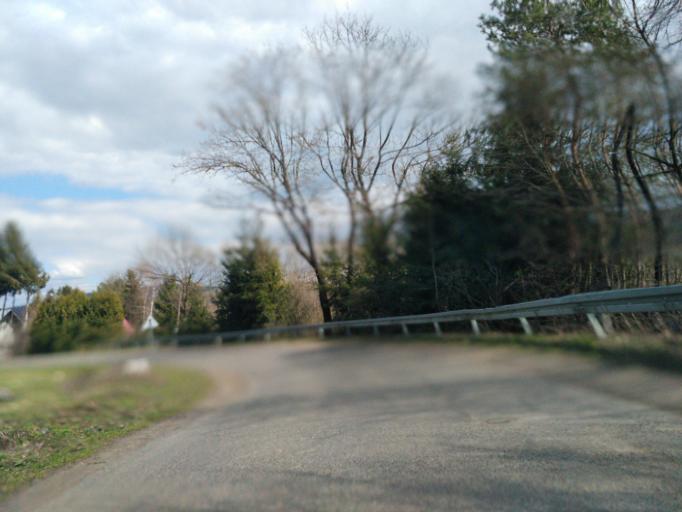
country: PL
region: Subcarpathian Voivodeship
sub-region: Powiat sanocki
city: Tyrawa Woloska
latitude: 49.6341
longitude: 22.2813
